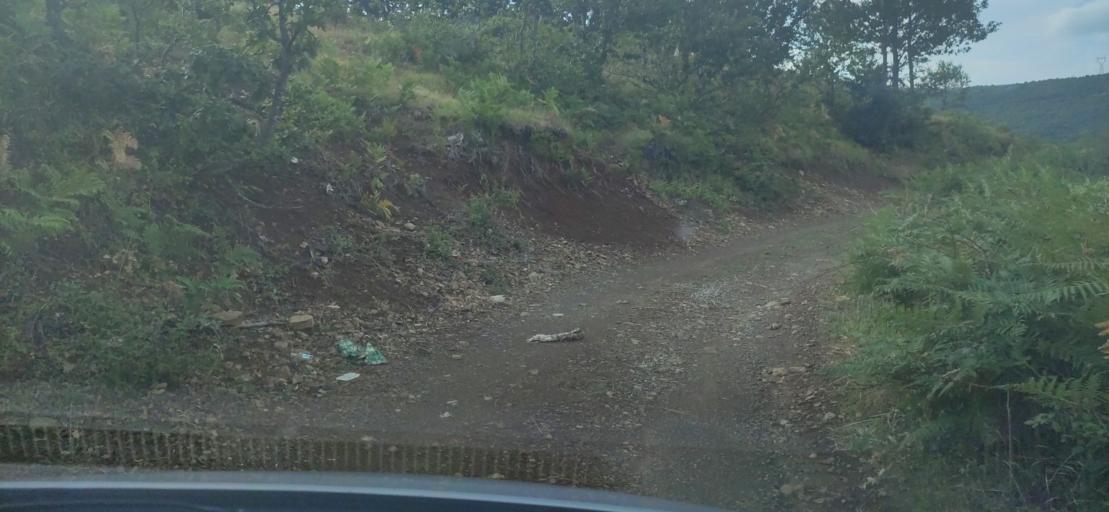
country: AL
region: Shkoder
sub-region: Rrethi i Pukes
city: Iballe
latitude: 42.1856
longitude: 19.9959
